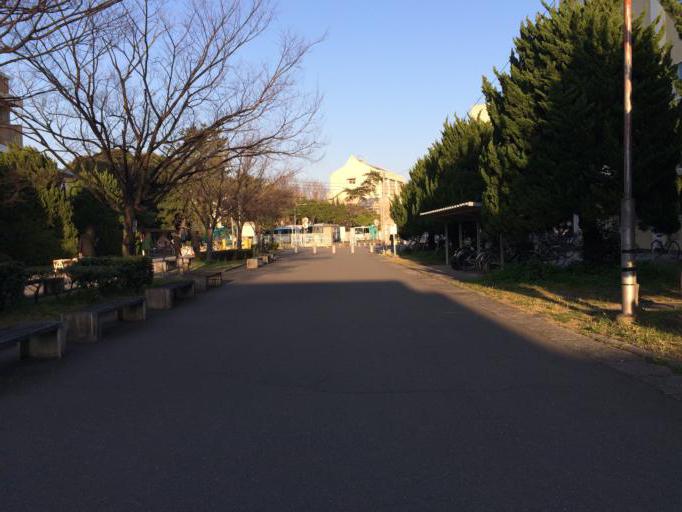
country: JP
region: Fukuoka
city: Fukuoka-shi
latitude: 33.6270
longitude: 130.4229
